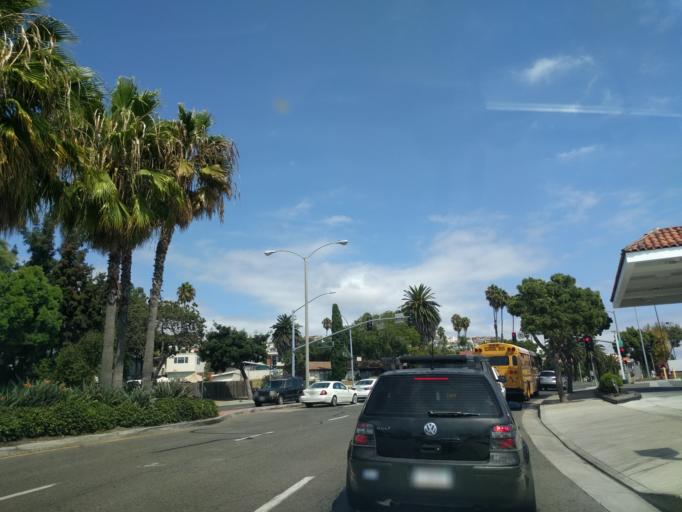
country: US
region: California
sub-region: Orange County
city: San Juan Capistrano
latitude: 33.4600
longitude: -117.6547
